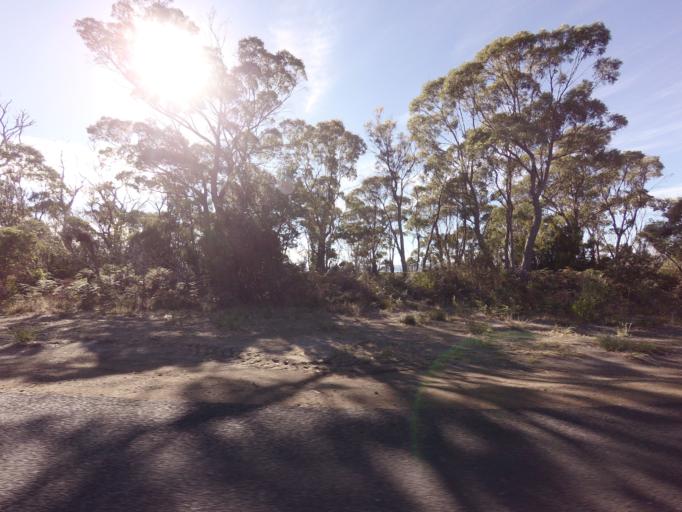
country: AU
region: Tasmania
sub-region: Clarence
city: Sandford
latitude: -43.0097
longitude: 147.7090
